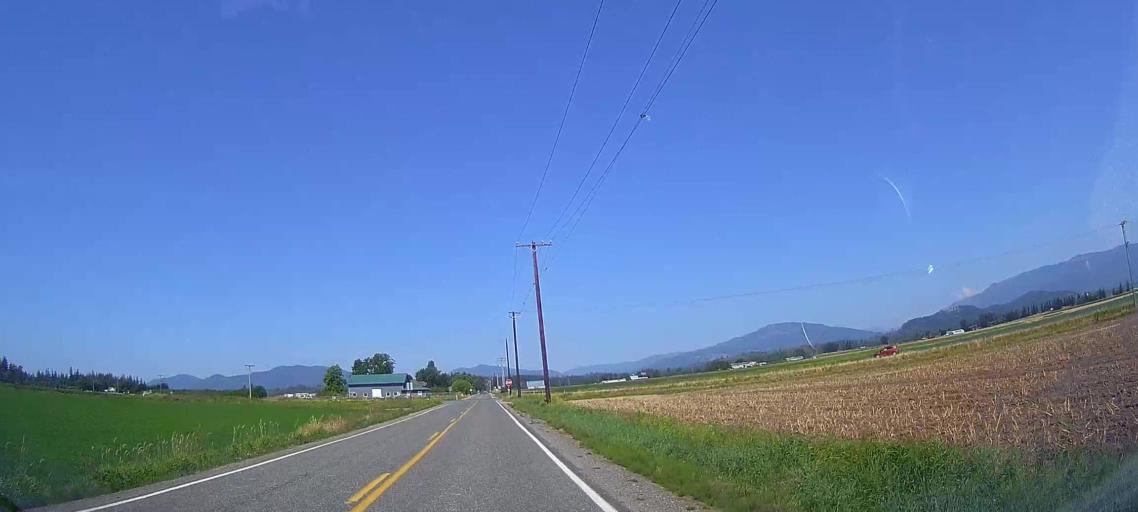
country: US
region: Washington
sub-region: Skagit County
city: Burlington
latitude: 48.4989
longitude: -122.3572
